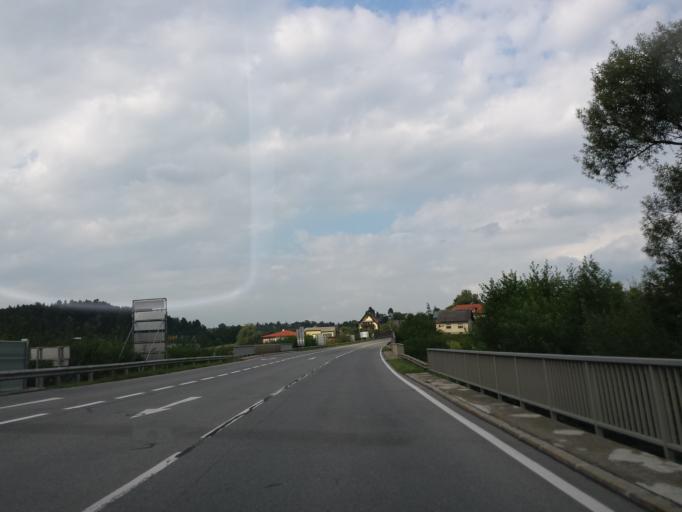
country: AT
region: Styria
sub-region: Politischer Bezirk Deutschlandsberg
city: Stainz
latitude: 46.8977
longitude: 15.2697
